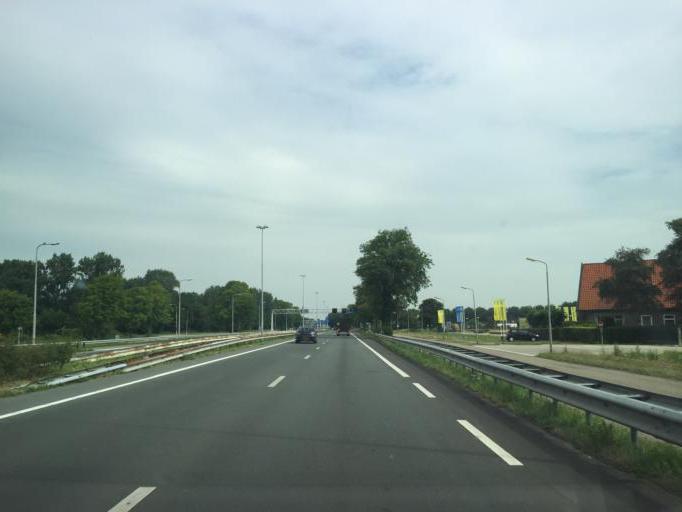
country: NL
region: North Holland
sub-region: Gemeente Velsen
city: Velsen-Zuid
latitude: 52.4409
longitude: 4.6517
